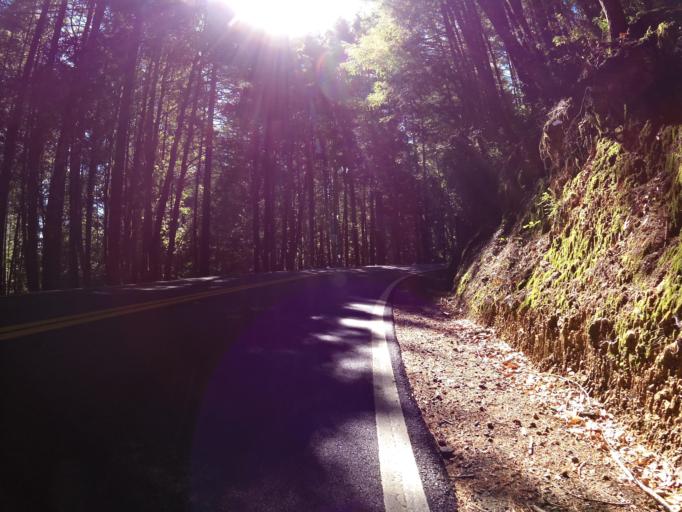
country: US
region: California
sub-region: Humboldt County
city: Redway
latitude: 39.8519
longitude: -123.7357
